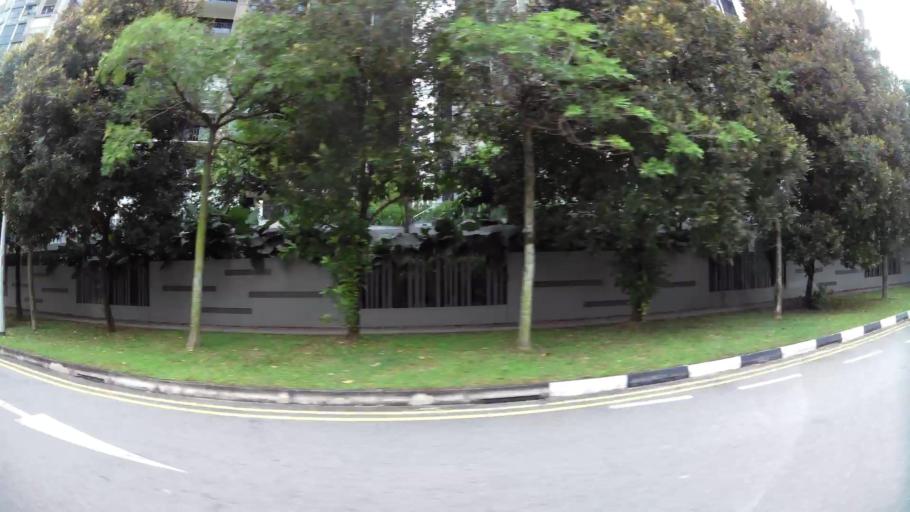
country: MY
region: Johor
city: Kampung Pasir Gudang Baru
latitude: 1.3976
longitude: 103.9135
